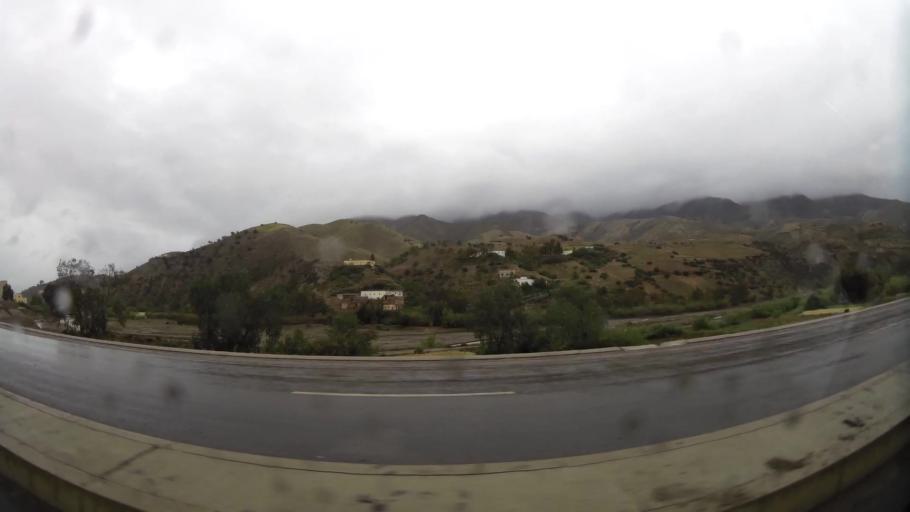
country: MA
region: Taza-Al Hoceima-Taounate
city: Imzourene
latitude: 35.0106
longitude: -3.8168
